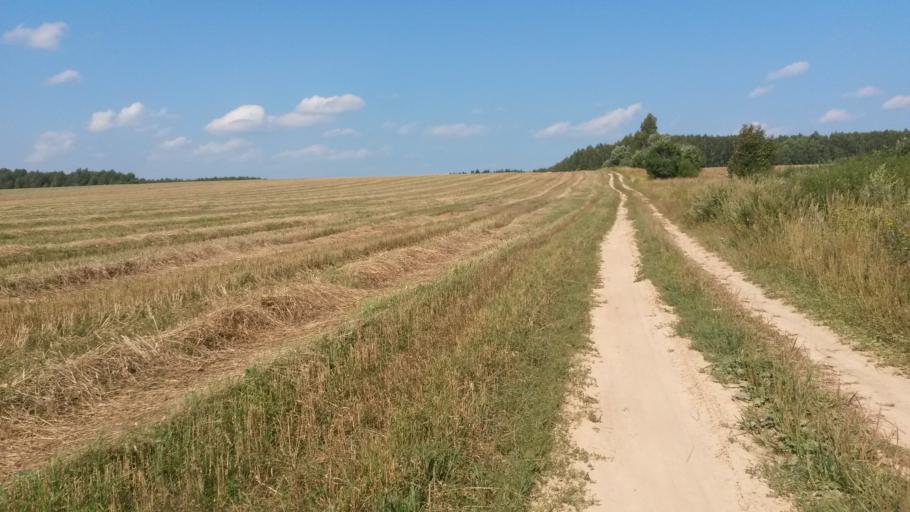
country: RU
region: Jaroslavl
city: Gavrilov-Yam
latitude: 57.3109
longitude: 39.9652
